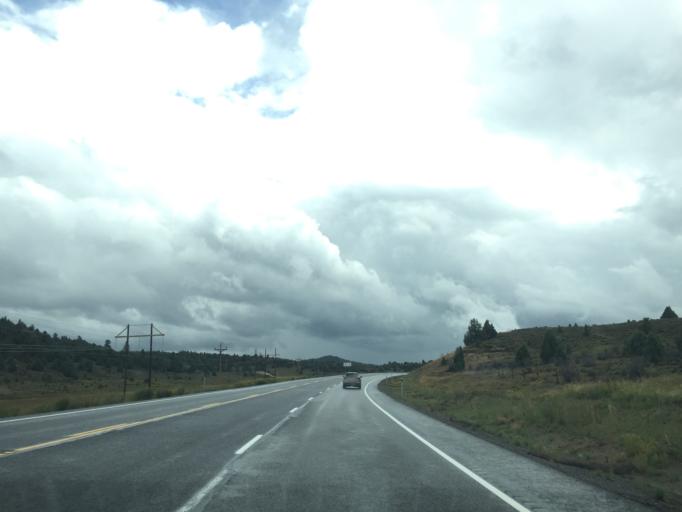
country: US
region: Utah
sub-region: Garfield County
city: Panguitch
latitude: 37.5107
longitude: -112.4976
